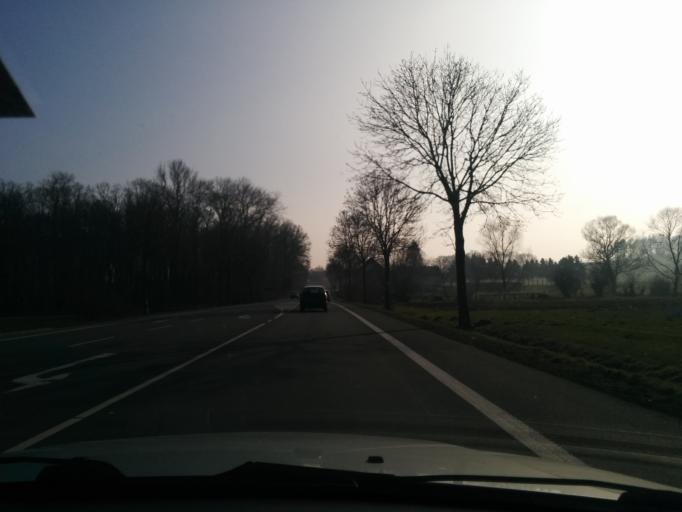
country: DE
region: North Rhine-Westphalia
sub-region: Regierungsbezirk Detmold
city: Steinheim
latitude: 51.8337
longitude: 9.0784
